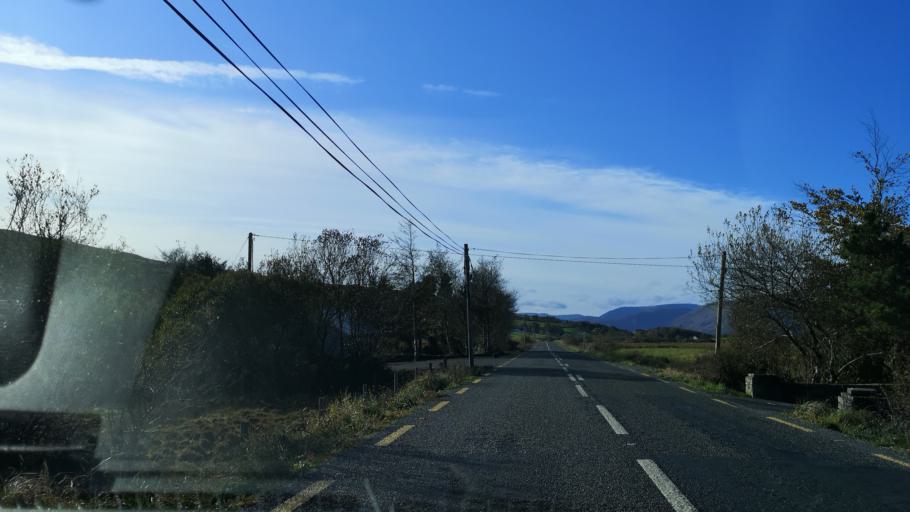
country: IE
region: Connaught
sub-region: Maigh Eo
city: Westport
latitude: 53.7162
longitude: -9.5467
